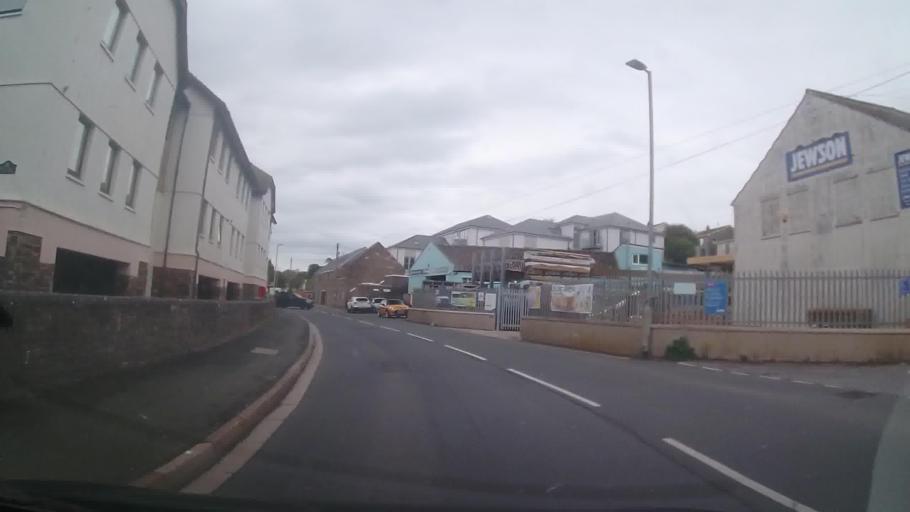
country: GB
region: England
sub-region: Devon
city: Kingsbridge
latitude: 50.2772
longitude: -3.7722
